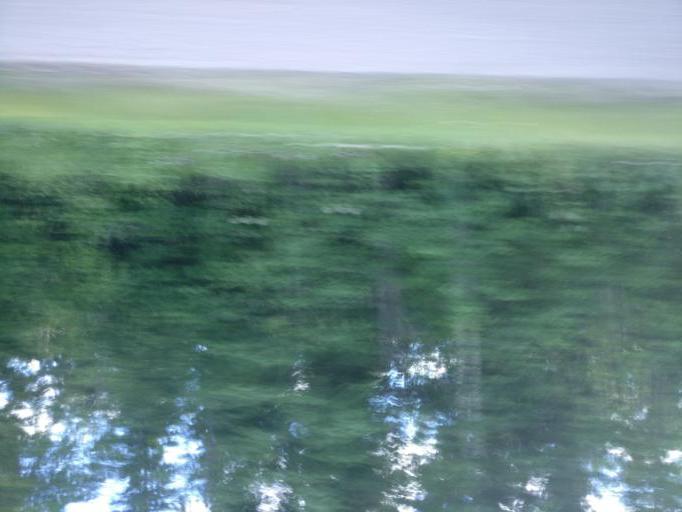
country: FI
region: Uusimaa
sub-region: Helsinki
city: Vihti
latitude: 60.4366
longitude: 24.4843
